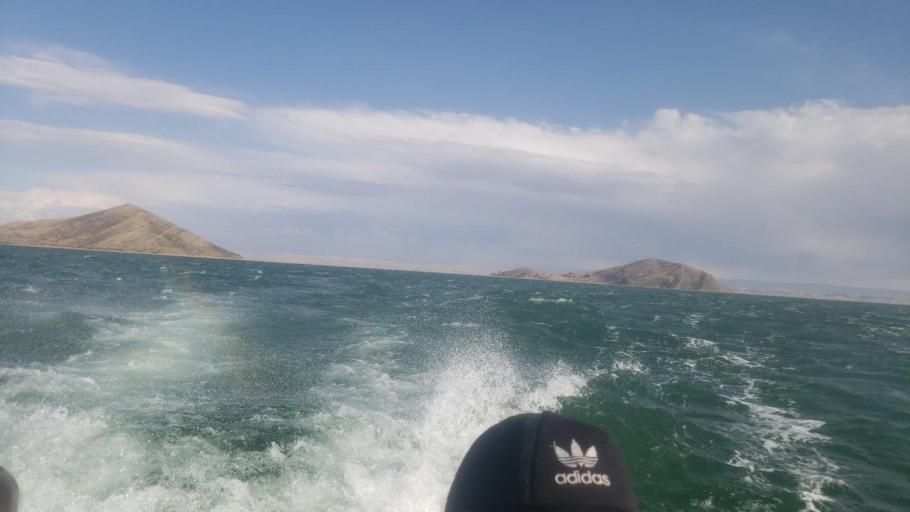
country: BO
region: La Paz
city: Huatajata
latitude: -16.3156
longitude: -68.7421
